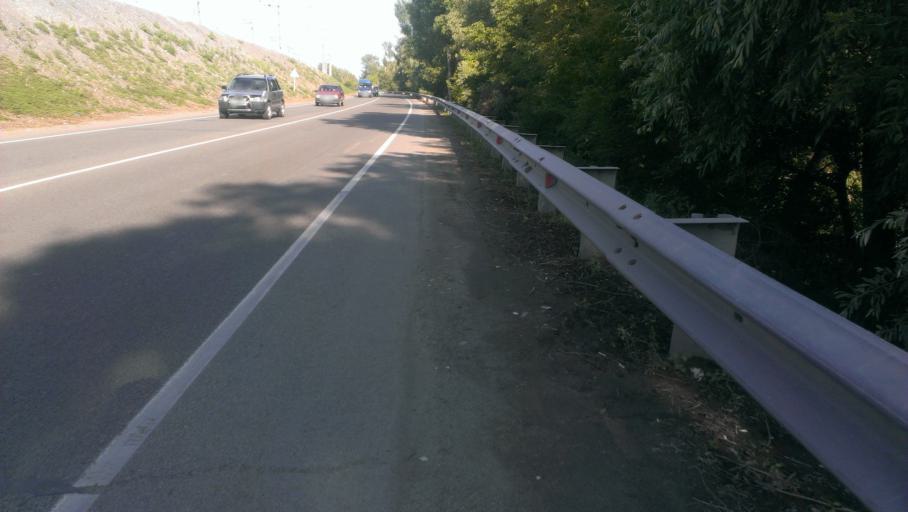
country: RU
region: Altai Krai
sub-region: Gorod Barnaulskiy
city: Barnaul
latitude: 53.3672
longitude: 83.8370
